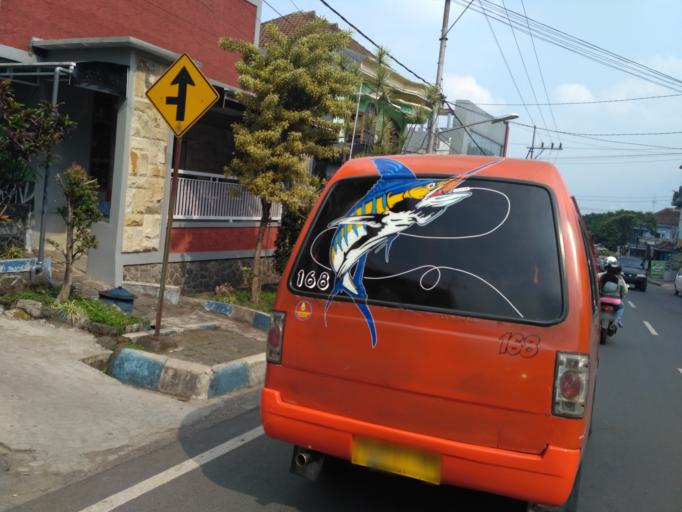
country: ID
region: East Java
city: Batu
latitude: -7.8366
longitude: 112.5285
